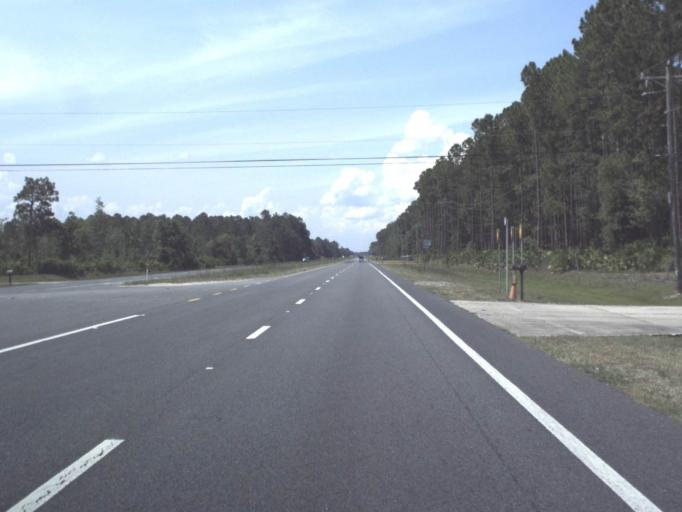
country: US
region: Florida
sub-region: Clay County
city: Green Cove Springs
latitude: 29.8432
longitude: -81.6619
